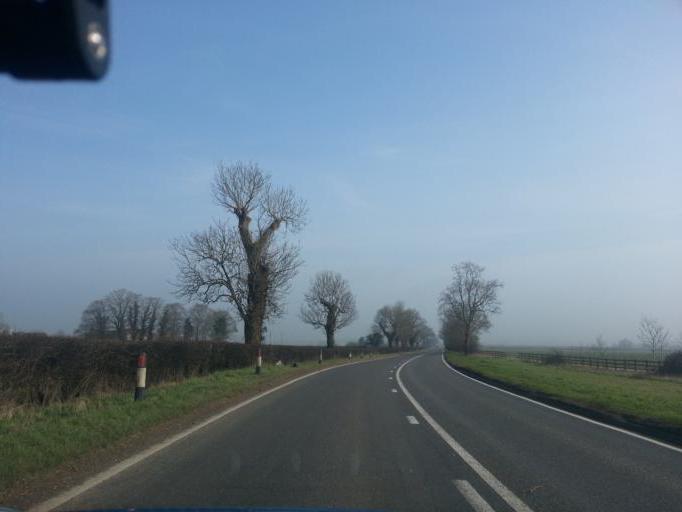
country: GB
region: England
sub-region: Oxfordshire
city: Shrivenham
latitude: 51.6236
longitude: -1.6258
